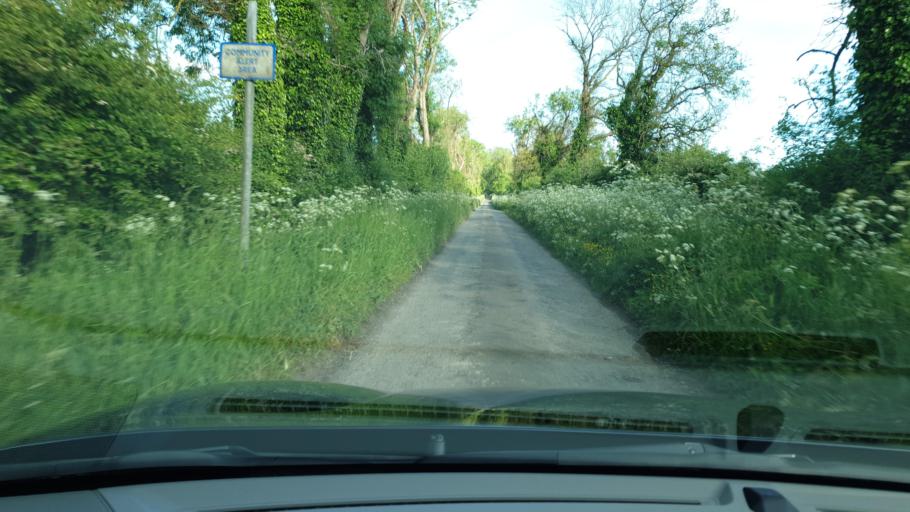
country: IE
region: Leinster
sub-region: An Mhi
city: Ashbourne
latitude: 53.5558
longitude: -6.4297
